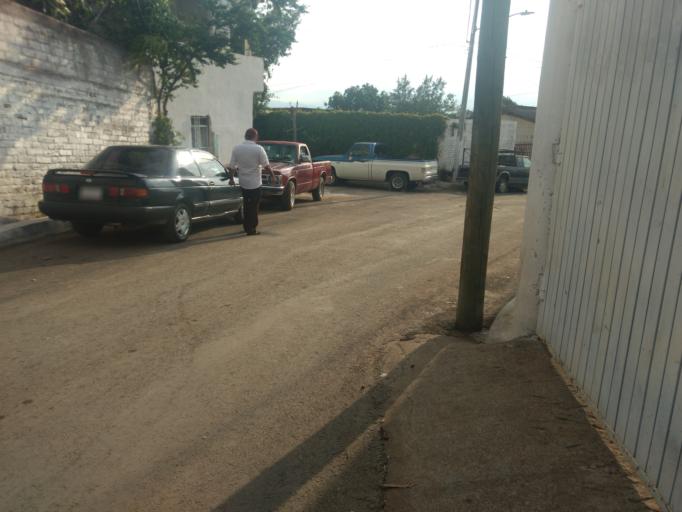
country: MX
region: Nayarit
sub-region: Tepic
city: La Corregidora
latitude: 21.4656
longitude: -104.8008
